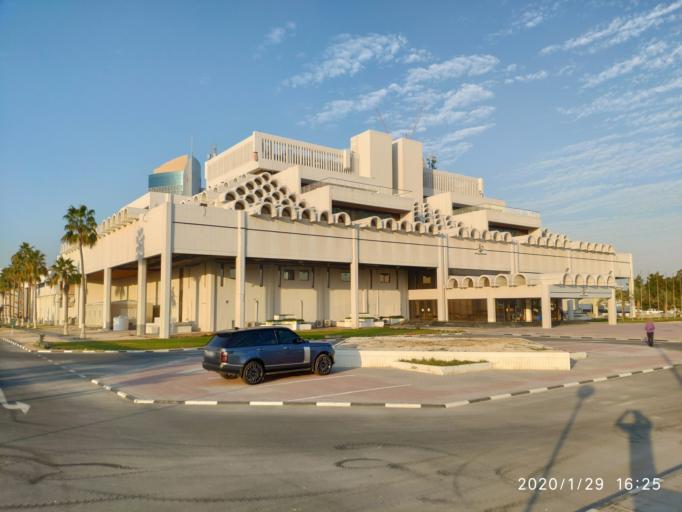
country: QA
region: Baladiyat ad Dawhah
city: Doha
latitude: 25.3095
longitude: 51.5165
